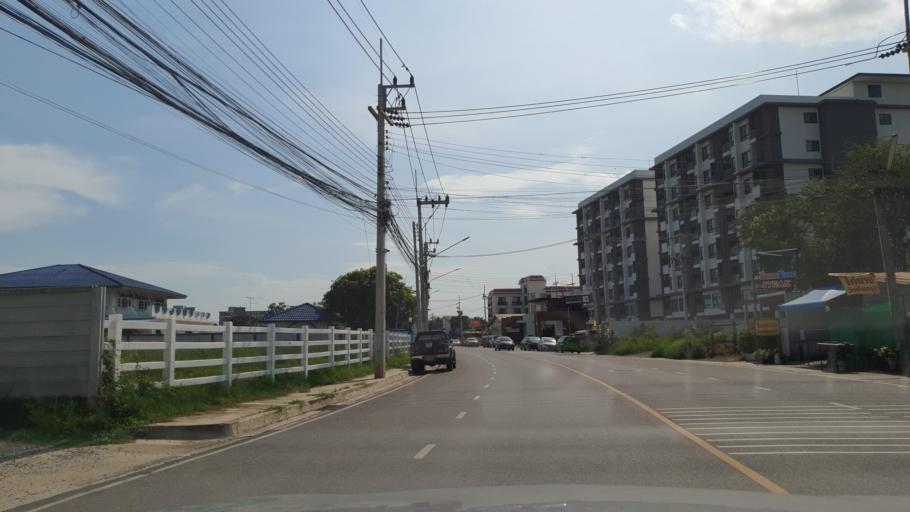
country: TH
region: Chachoengsao
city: Chachoengsao
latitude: 13.6779
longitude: 101.0596
